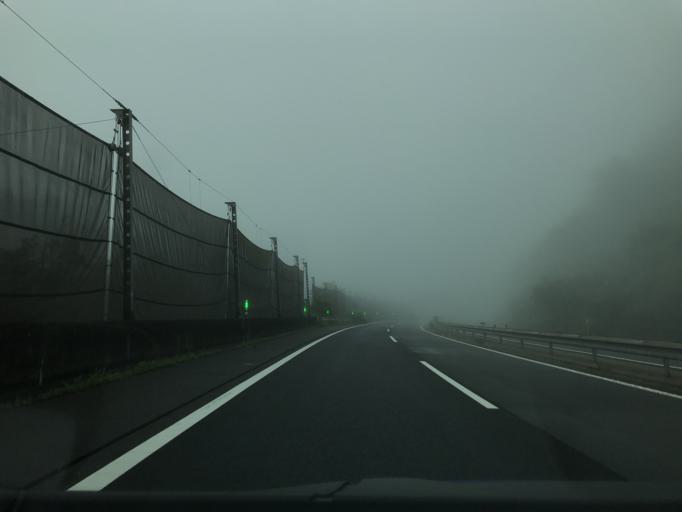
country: JP
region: Oita
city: Hiji
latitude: 33.3598
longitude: 131.4505
